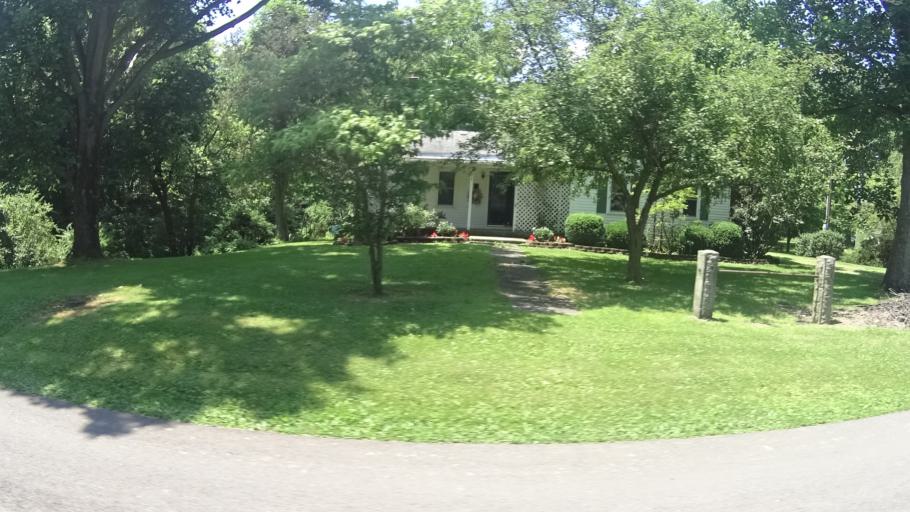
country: US
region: Ohio
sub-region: Erie County
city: Huron
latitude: 41.3234
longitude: -82.5204
